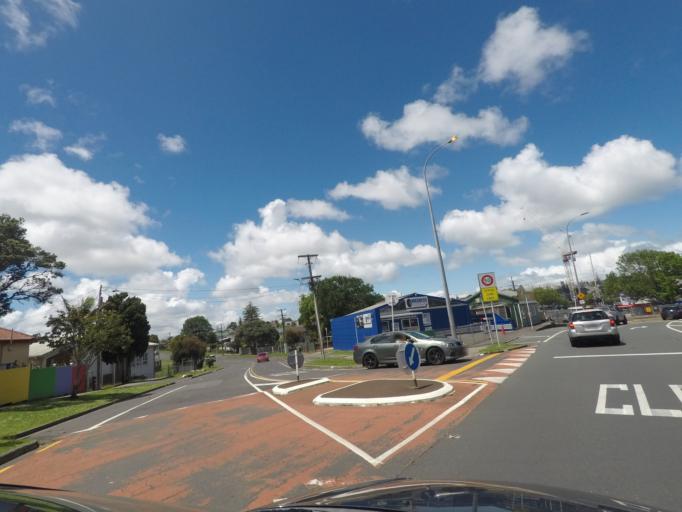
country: NZ
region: Auckland
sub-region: Auckland
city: Waitakere
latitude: -36.9095
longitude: 174.6522
